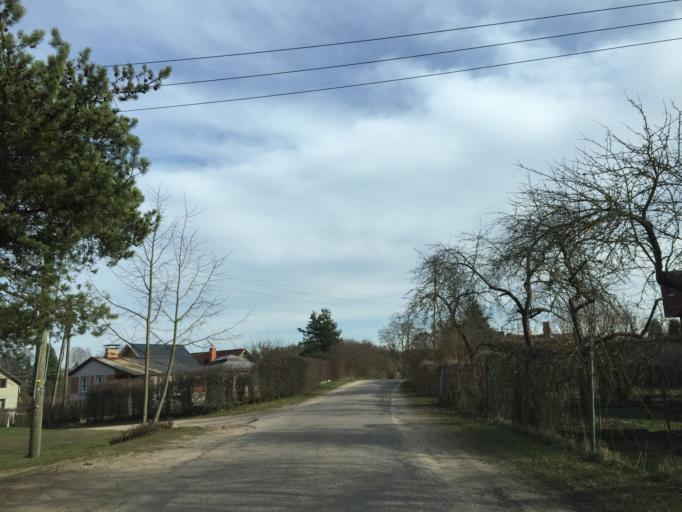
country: LV
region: Ogre
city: Ogre
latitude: 56.8098
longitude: 24.6350
